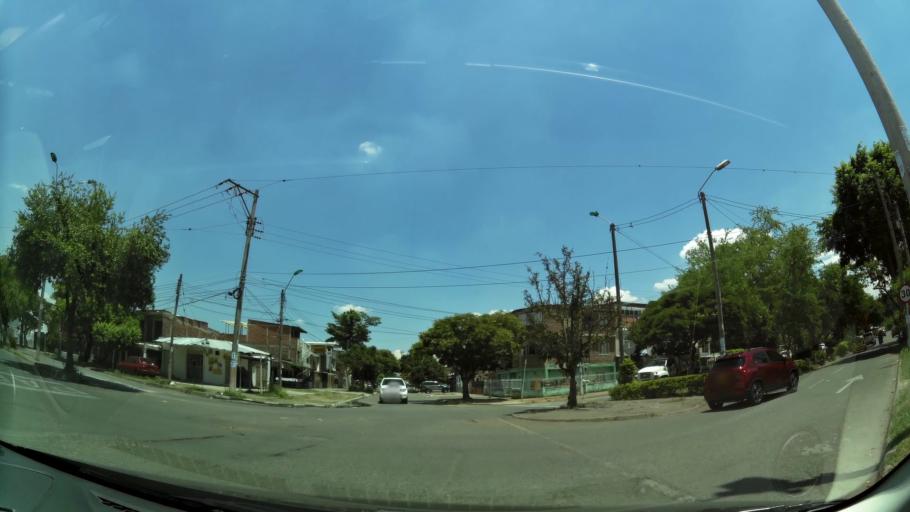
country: CO
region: Valle del Cauca
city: Cali
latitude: 3.4309
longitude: -76.5047
